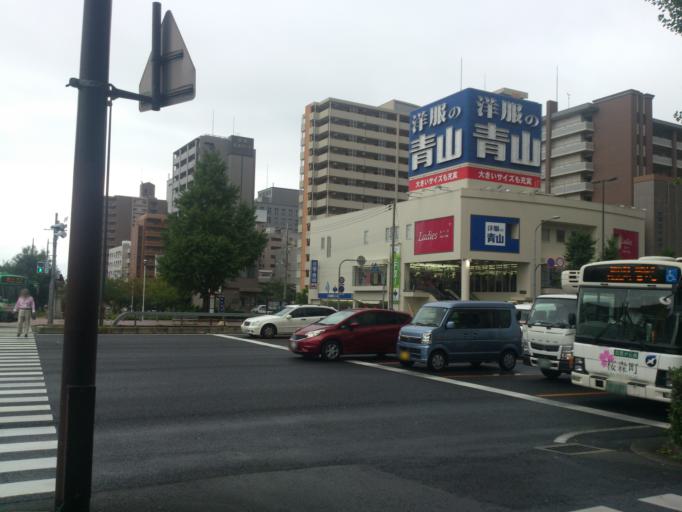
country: JP
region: Hyogo
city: Kobe
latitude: 34.6966
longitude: 135.2017
